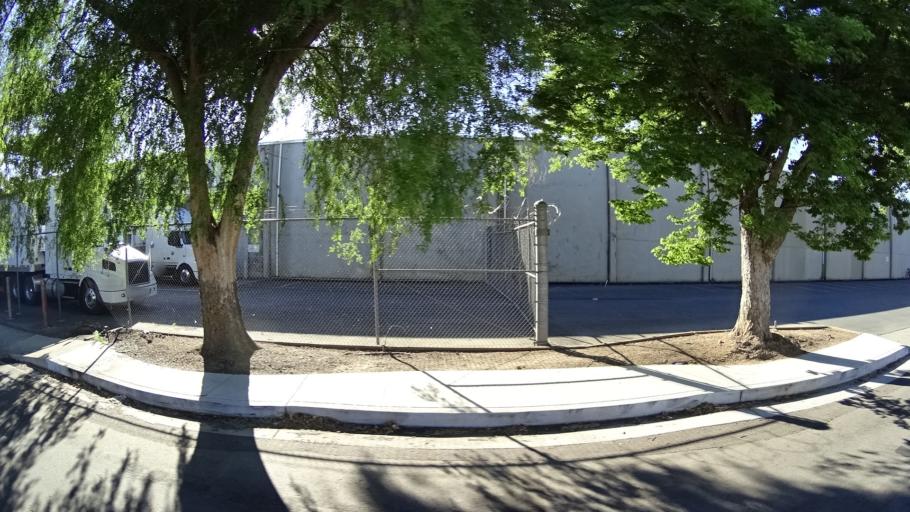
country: US
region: California
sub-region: Sacramento County
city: Sacramento
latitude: 38.5992
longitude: -121.4992
